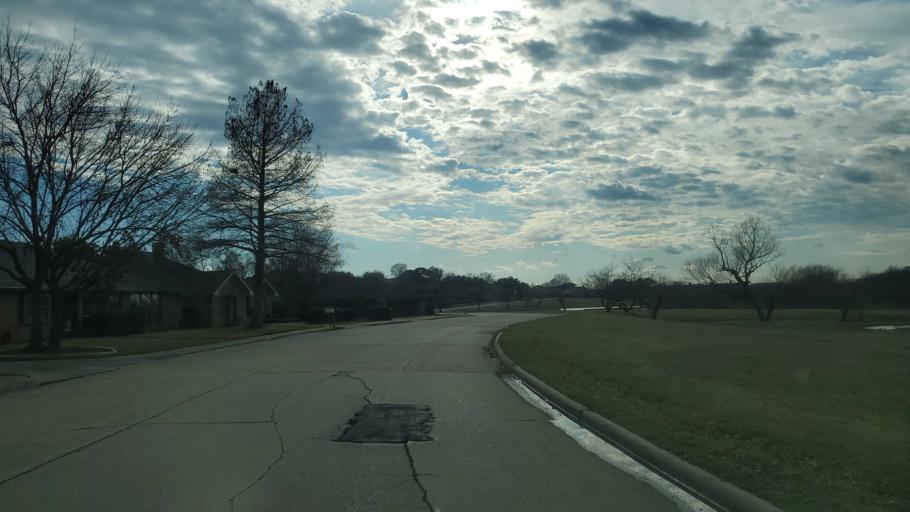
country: US
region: Texas
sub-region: Dallas County
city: Carrollton
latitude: 32.9928
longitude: -96.8948
